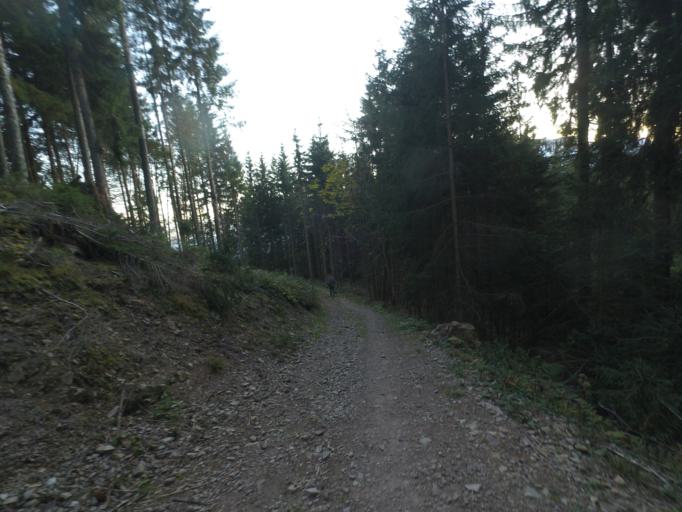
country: AT
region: Salzburg
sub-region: Politischer Bezirk Sankt Johann im Pongau
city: Pfarrwerfen
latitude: 47.4799
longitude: 13.2180
